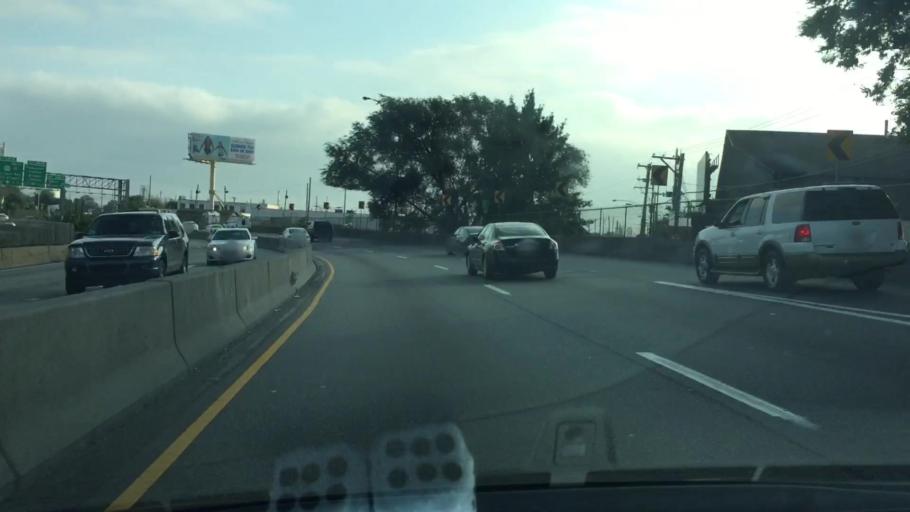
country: US
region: Pennsylvania
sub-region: Philadelphia County
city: Philadelphia
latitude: 39.9330
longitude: -75.2001
